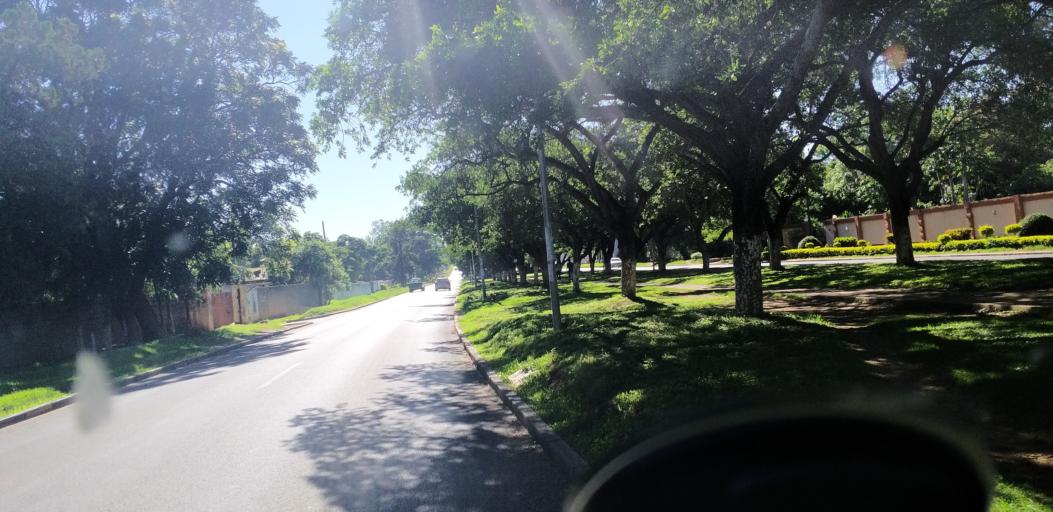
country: ZM
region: Lusaka
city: Lusaka
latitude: -15.4253
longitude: 28.3129
